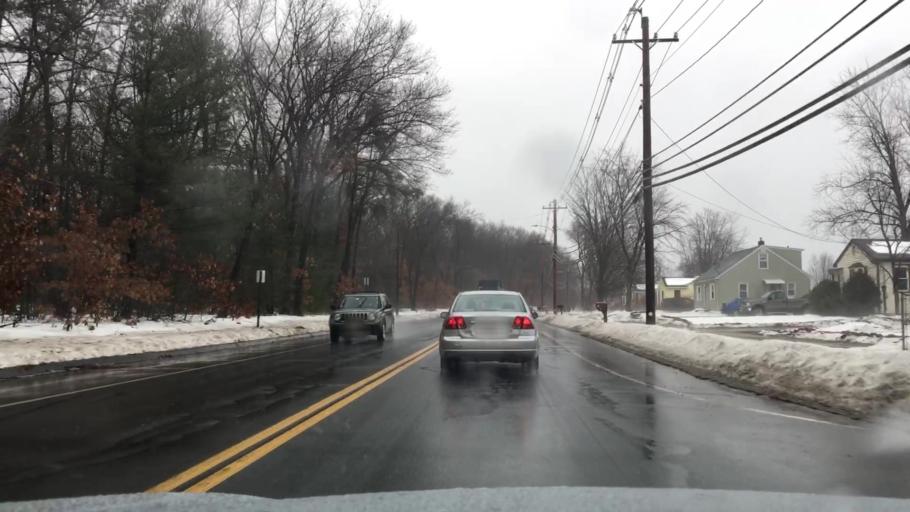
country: US
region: Massachusetts
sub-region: Hampden County
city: North Chicopee
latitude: 42.1704
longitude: -72.5407
